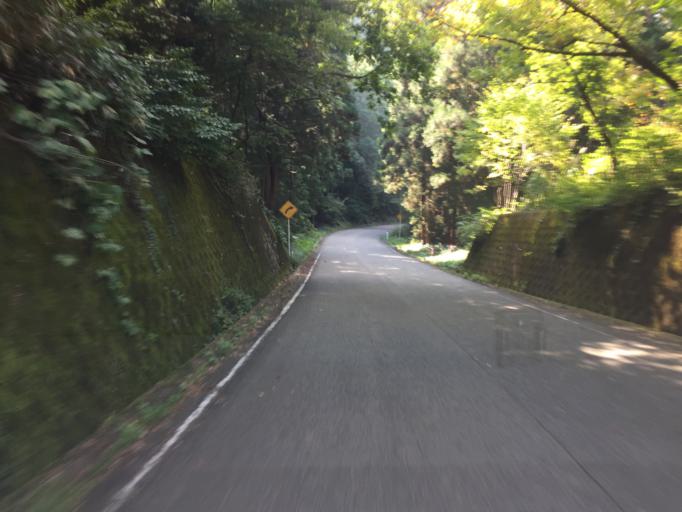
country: JP
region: Fukushima
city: Inawashiro
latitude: 37.4868
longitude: 139.9619
